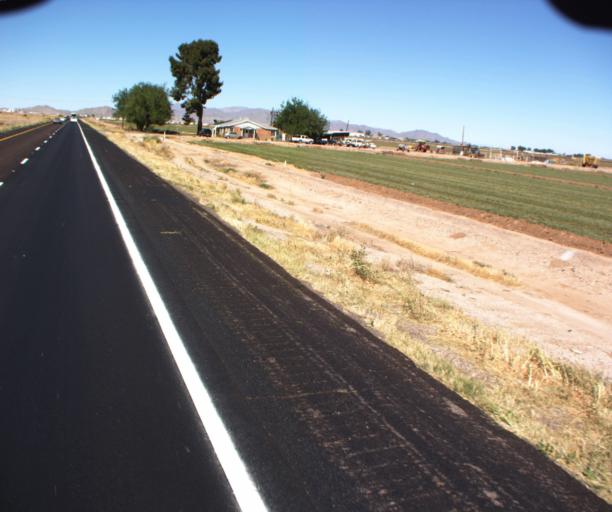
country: US
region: Arizona
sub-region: Maricopa County
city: Buckeye
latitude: 33.3582
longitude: -112.6251
